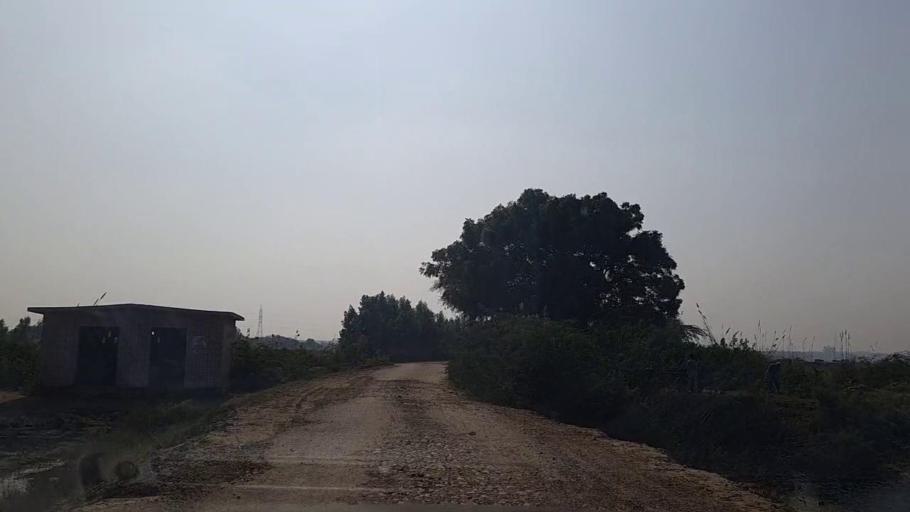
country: PK
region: Sindh
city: Mirpur Sakro
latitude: 24.5740
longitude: 67.7806
